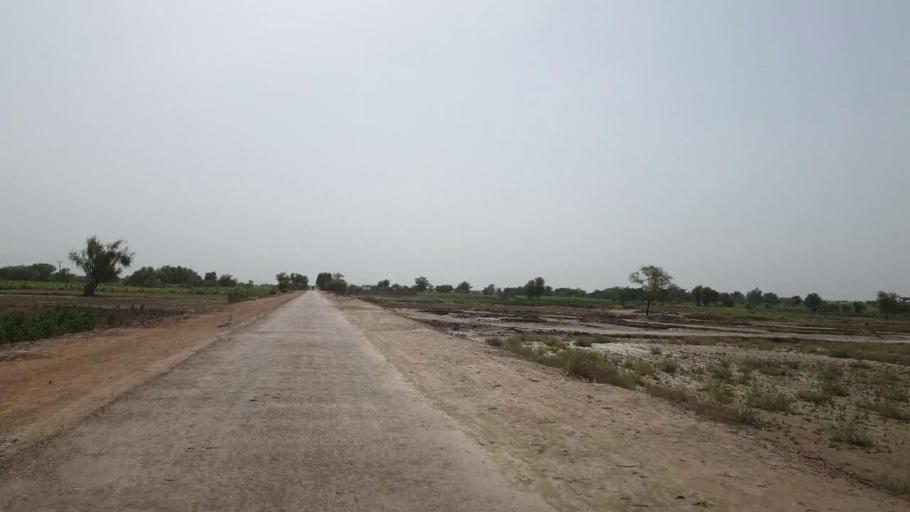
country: PK
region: Sindh
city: Bandhi
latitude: 26.5385
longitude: 68.4057
